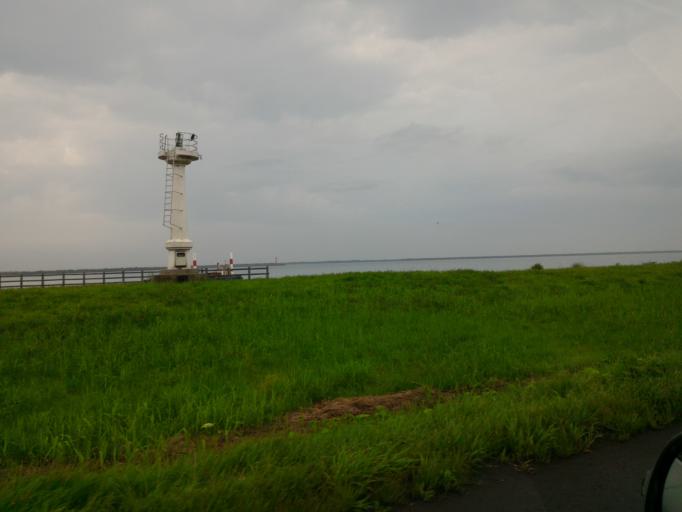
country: JP
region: Hokkaido
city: Rumoi
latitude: 43.9608
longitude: 141.6430
